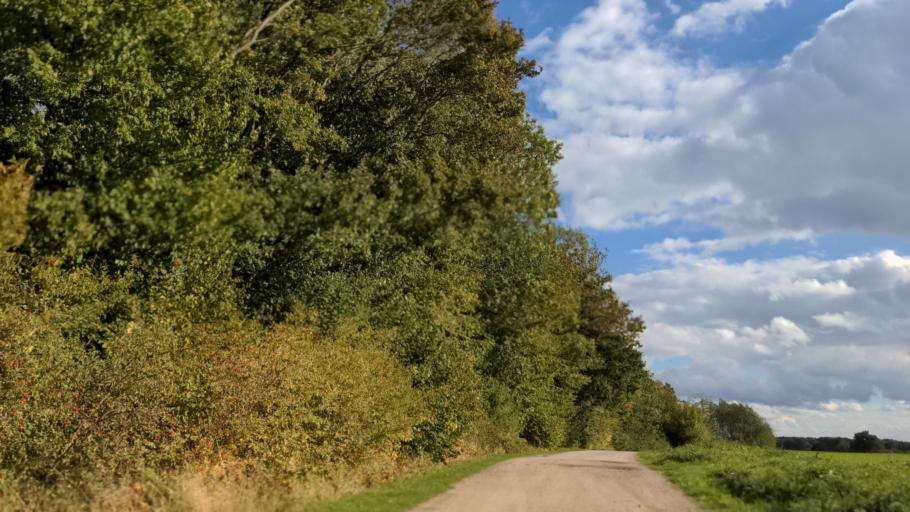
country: DE
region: Schleswig-Holstein
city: Monkhagen
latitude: 53.9376
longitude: 10.5809
